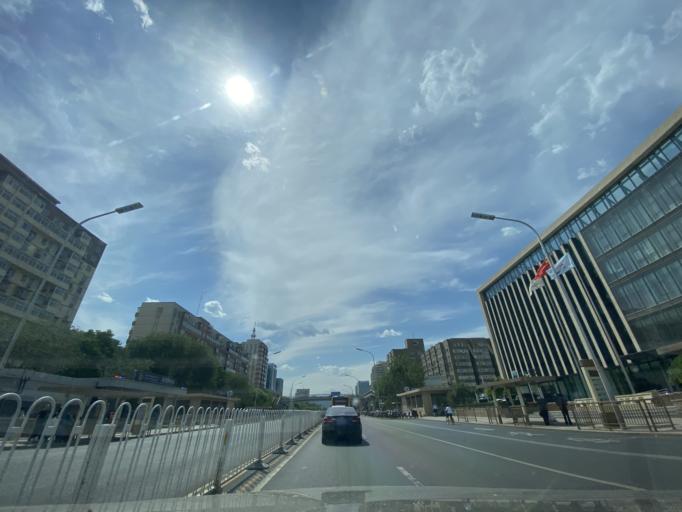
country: CN
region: Beijing
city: Lugu
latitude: 39.9062
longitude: 116.1844
